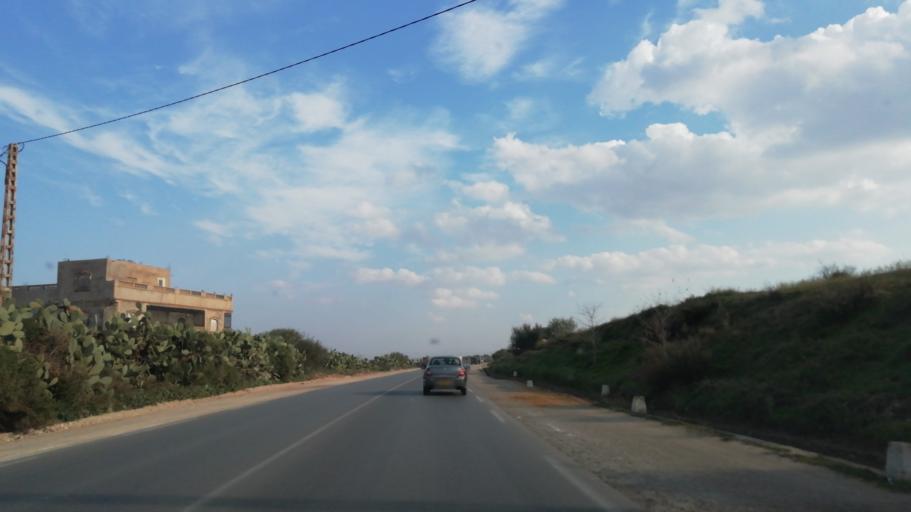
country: DZ
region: Relizane
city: Relizane
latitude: 35.9144
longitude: 0.4985
